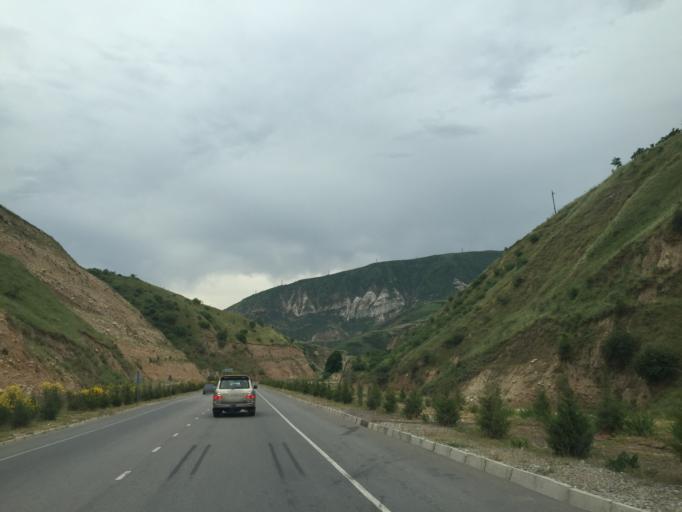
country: TJ
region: Khatlon
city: Norak
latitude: 38.4499
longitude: 69.2018
